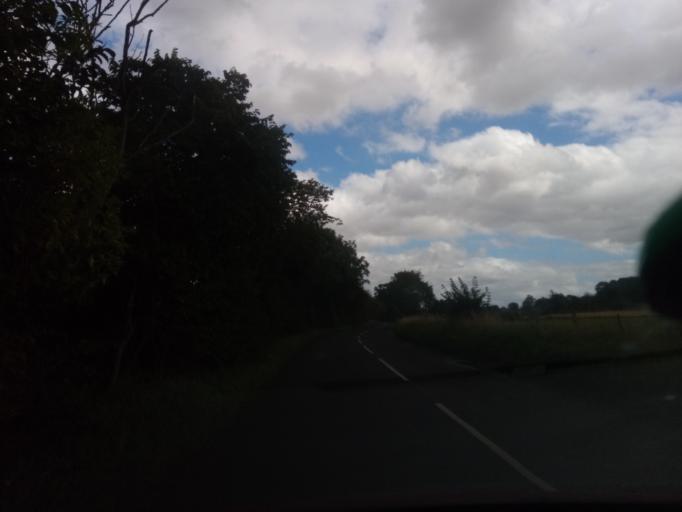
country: GB
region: Scotland
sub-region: The Scottish Borders
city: Kelso
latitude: 55.6004
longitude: -2.4175
